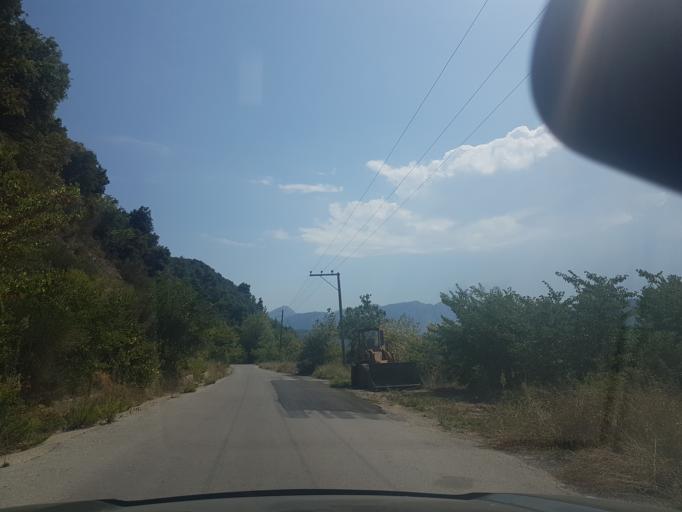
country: GR
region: Central Greece
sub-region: Nomos Evvoias
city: Kymi
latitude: 38.6499
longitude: 23.9059
